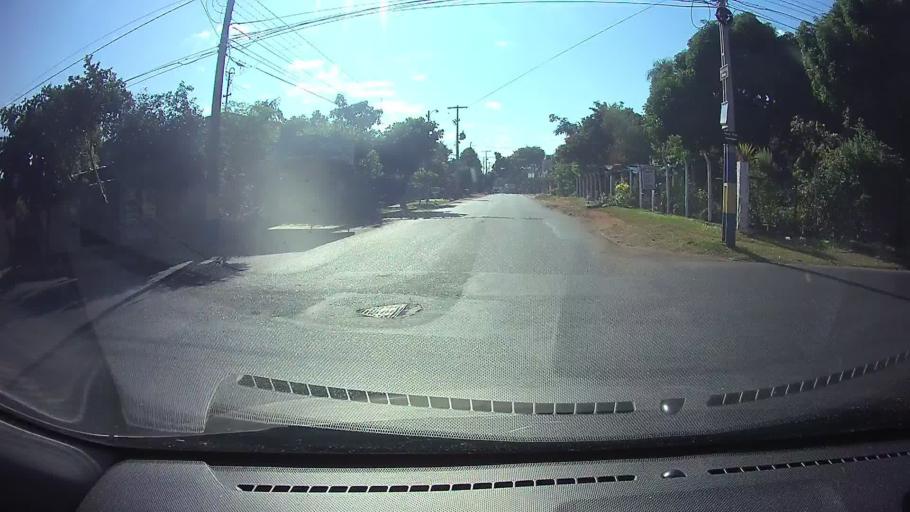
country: PY
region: Central
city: San Lorenzo
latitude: -25.2765
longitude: -57.5008
